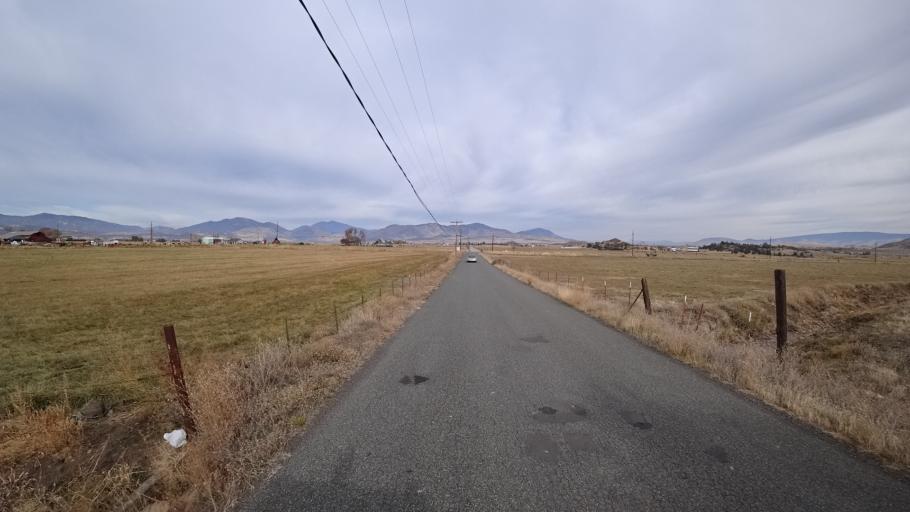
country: US
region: California
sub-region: Siskiyou County
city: Montague
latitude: 41.7041
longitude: -122.5496
